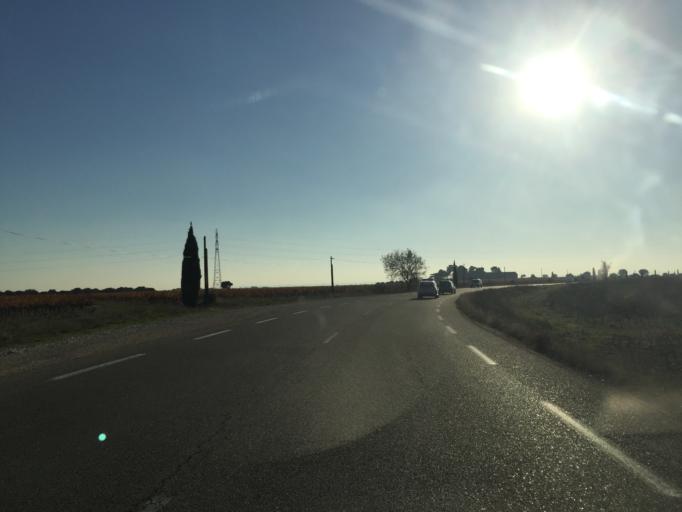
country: FR
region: Provence-Alpes-Cote d'Azur
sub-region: Departement du Vaucluse
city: Sainte-Cecile-les-Vignes
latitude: 44.2203
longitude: 4.8780
